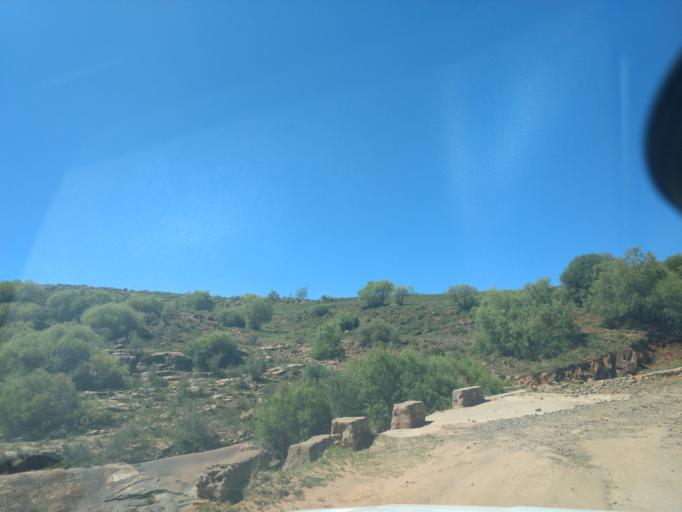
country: LS
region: Maseru
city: Maseru
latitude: -29.4828
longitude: 27.3706
